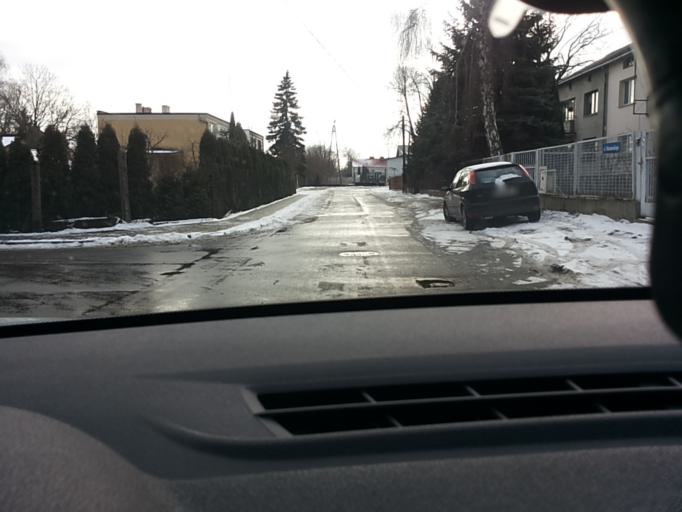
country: PL
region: Lodz Voivodeship
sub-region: Skierniewice
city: Skierniewice
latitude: 51.9597
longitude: 20.1358
